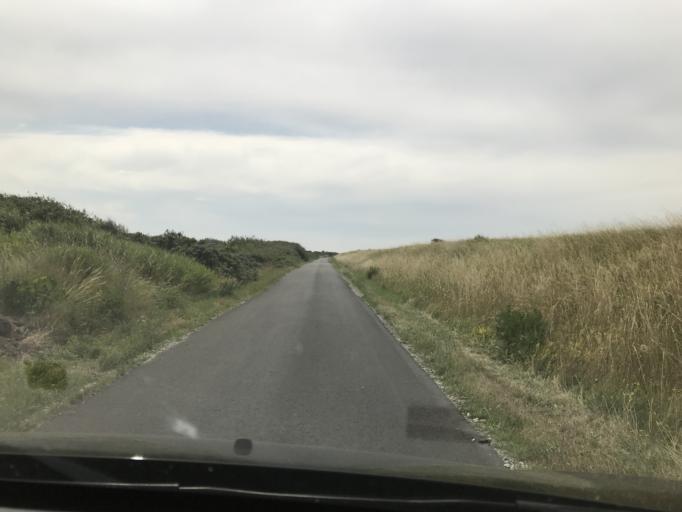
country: DK
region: South Denmark
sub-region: Faaborg-Midtfyn Kommune
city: Faaborg
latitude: 54.9302
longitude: 10.2453
